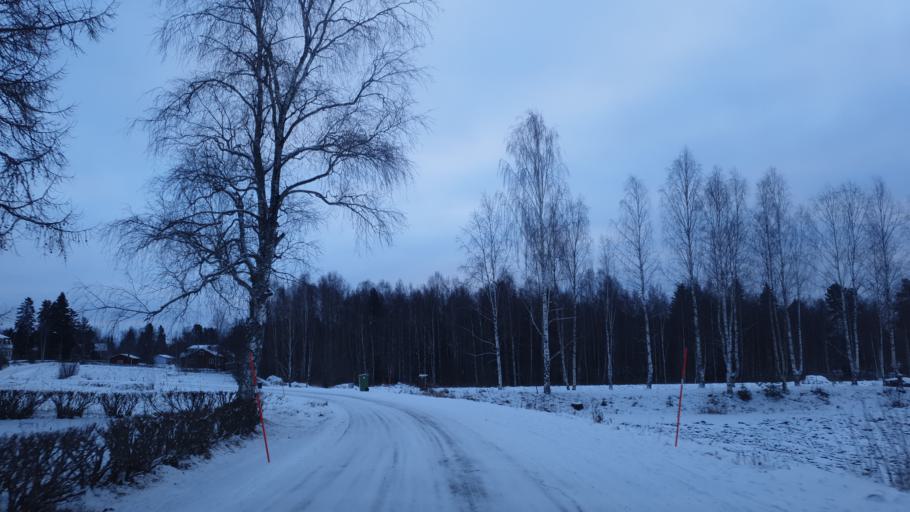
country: SE
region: Gaevleborg
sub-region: Bollnas Kommun
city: Kilafors
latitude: 61.2533
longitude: 16.5449
